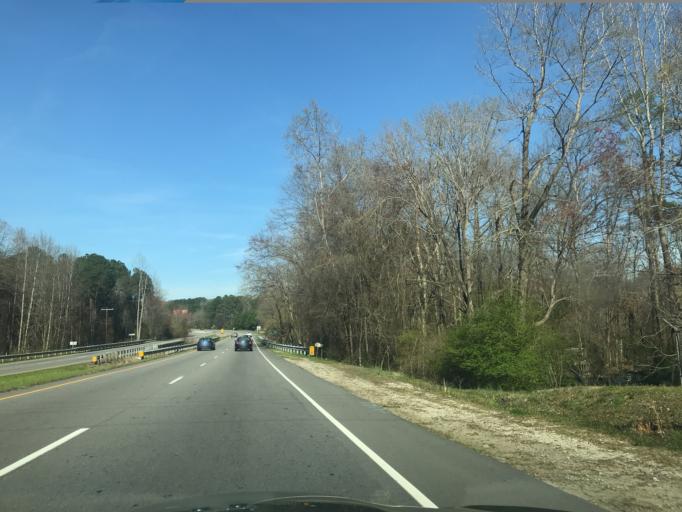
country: US
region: North Carolina
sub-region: Wake County
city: Garner
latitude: 35.6869
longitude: -78.6819
